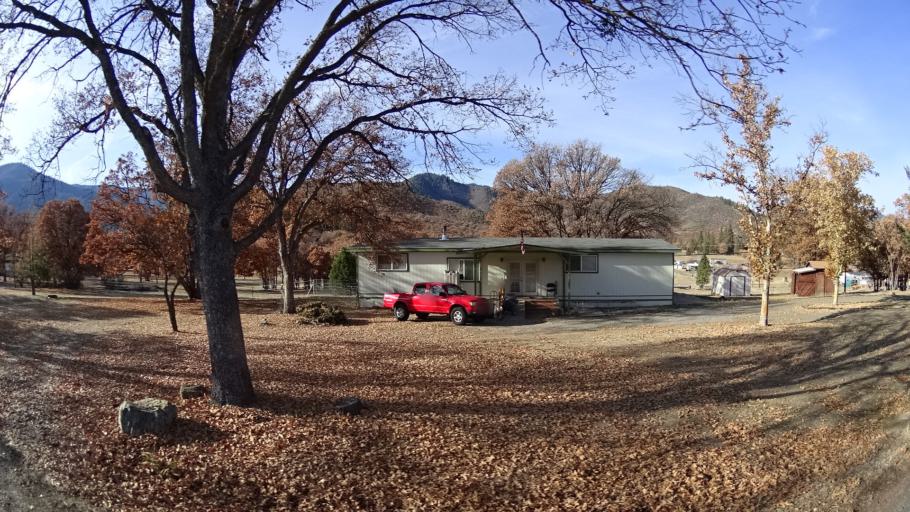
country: US
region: California
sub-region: Siskiyou County
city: Yreka
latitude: 41.6679
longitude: -122.6220
